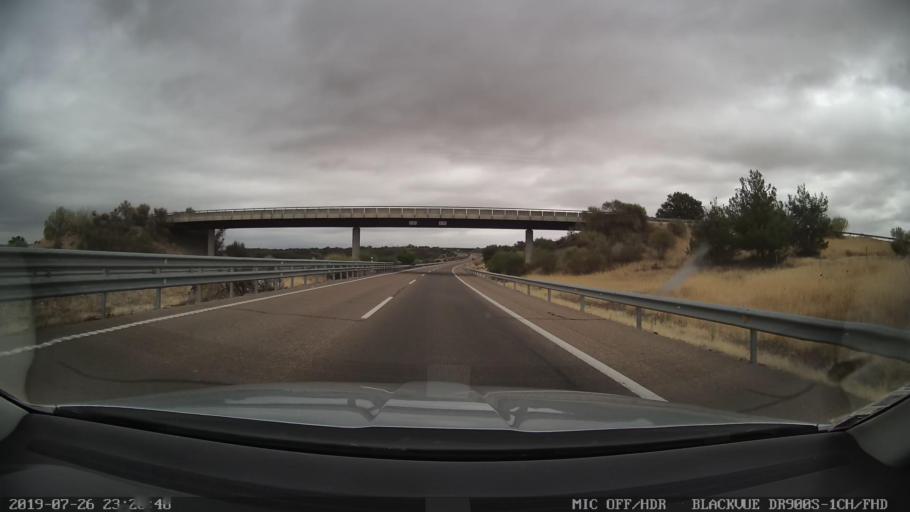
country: ES
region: Extremadura
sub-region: Provincia de Caceres
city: Villamesias
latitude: 39.2517
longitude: -5.8747
